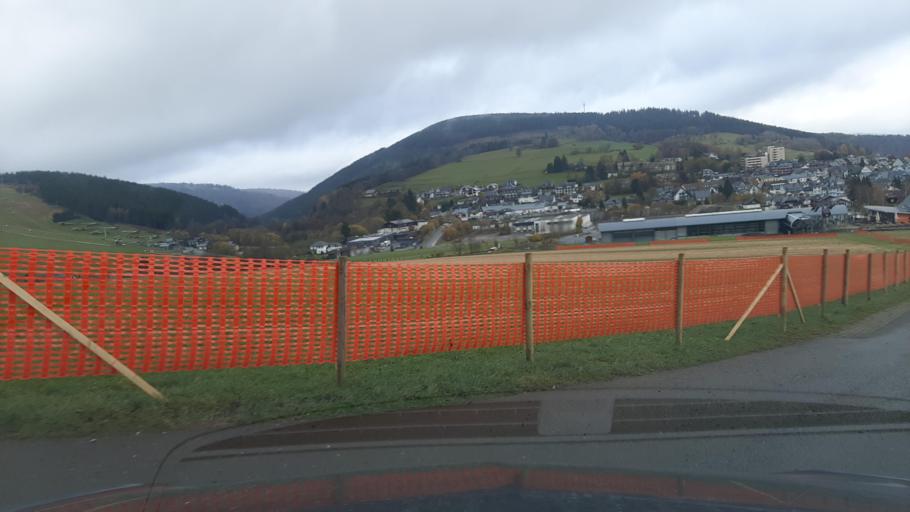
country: DE
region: Hesse
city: Willingen
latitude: 51.2886
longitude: 8.6016
